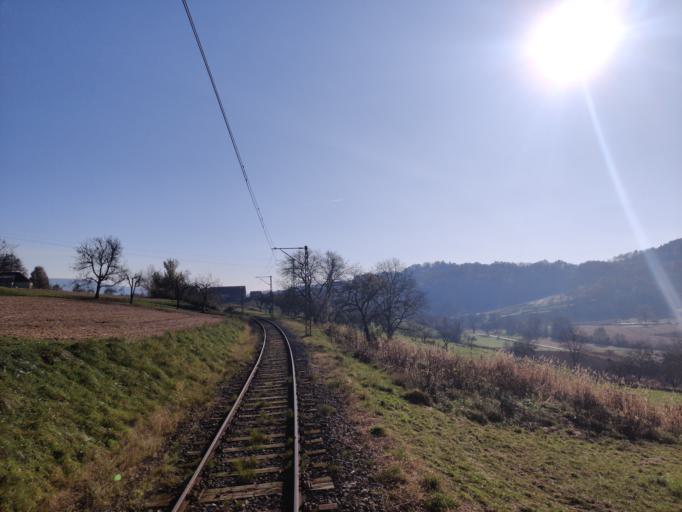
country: AT
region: Styria
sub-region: Politischer Bezirk Suedoststeiermark
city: Trautmannsdorf in Oststeiermark
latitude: 46.8827
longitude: 15.8828
